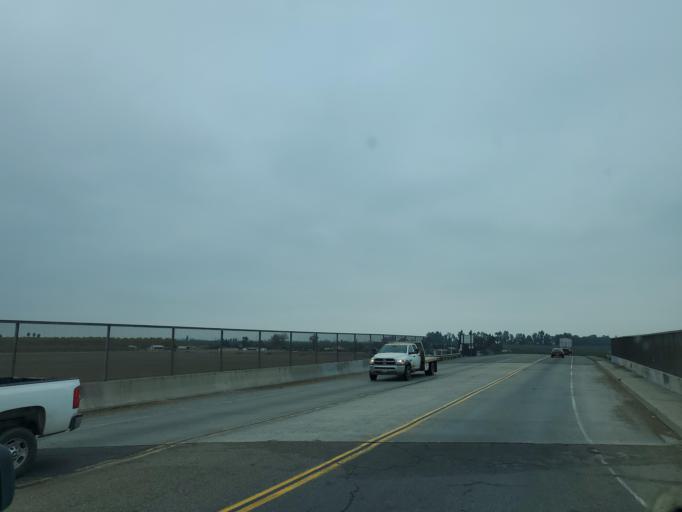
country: US
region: California
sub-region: Stanislaus County
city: Keyes
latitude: 37.5477
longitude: -120.9070
